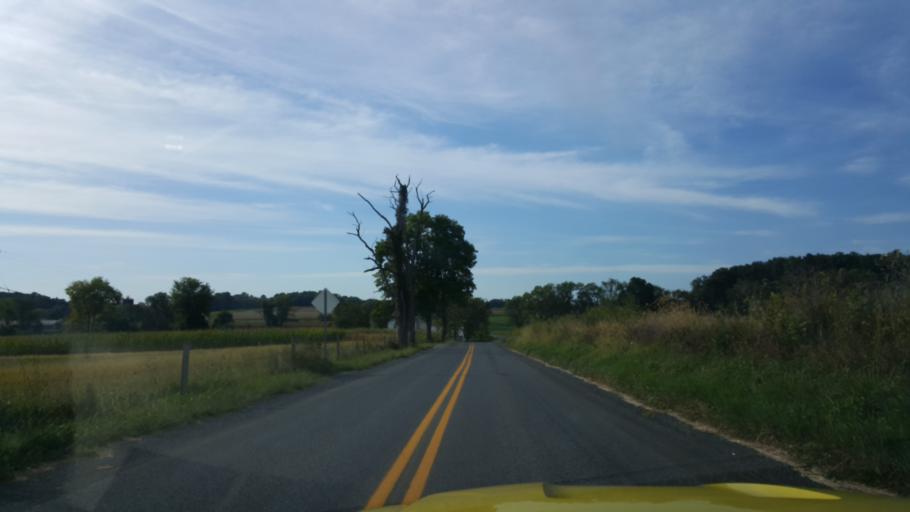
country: US
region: Pennsylvania
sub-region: Lebanon County
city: Campbelltown
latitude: 40.2351
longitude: -76.5806
